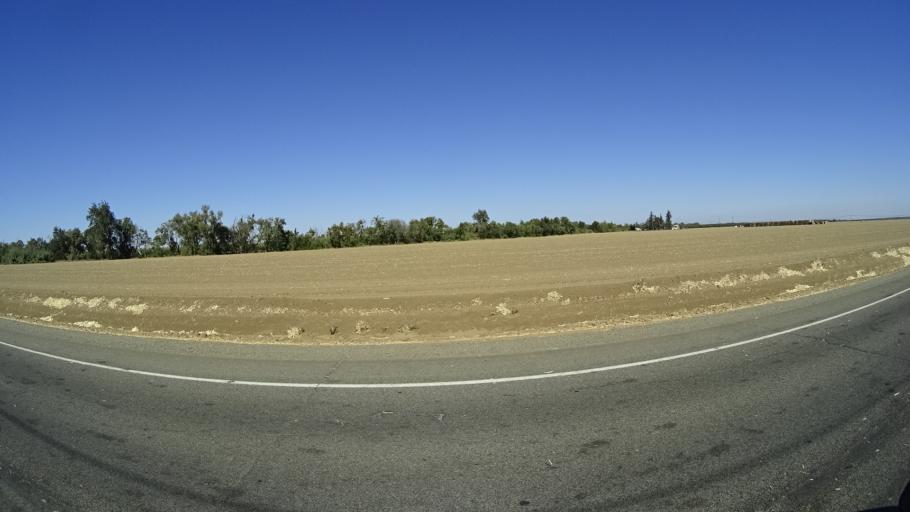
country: US
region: California
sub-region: Yolo County
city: Davis
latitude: 38.5613
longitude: -121.8440
